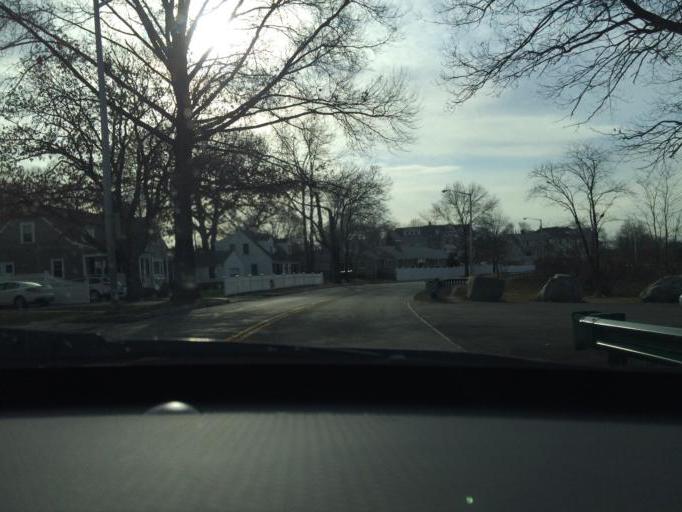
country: US
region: Massachusetts
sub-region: Norfolk County
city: Quincy
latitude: 42.2622
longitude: -71.0006
